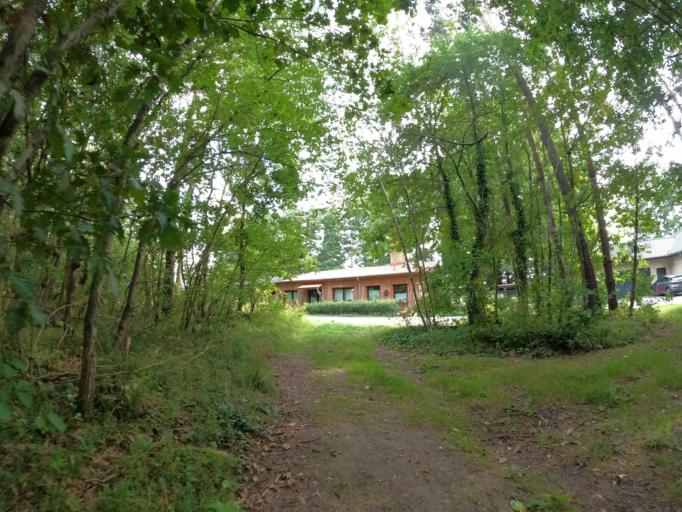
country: DE
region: Mecklenburg-Vorpommern
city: Klink
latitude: 53.5101
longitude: 12.6336
